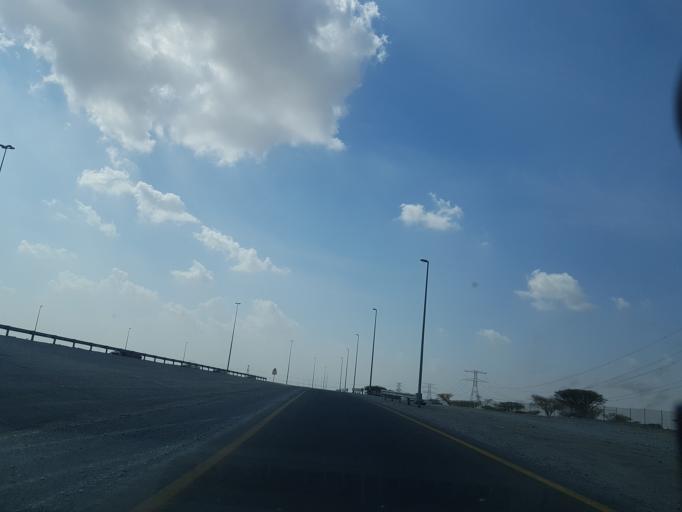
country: AE
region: Ra's al Khaymah
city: Ras al-Khaimah
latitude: 25.7612
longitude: 56.0210
